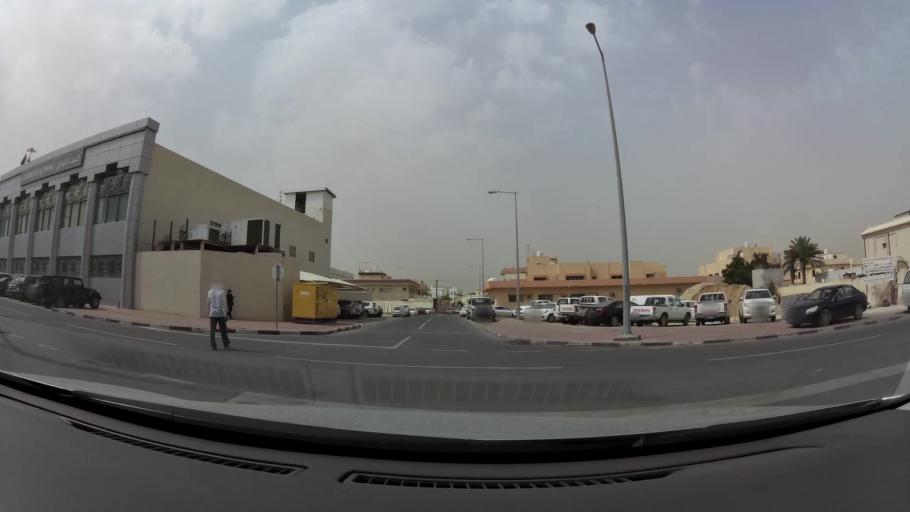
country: QA
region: Baladiyat ad Dawhah
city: Doha
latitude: 25.2581
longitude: 51.5499
